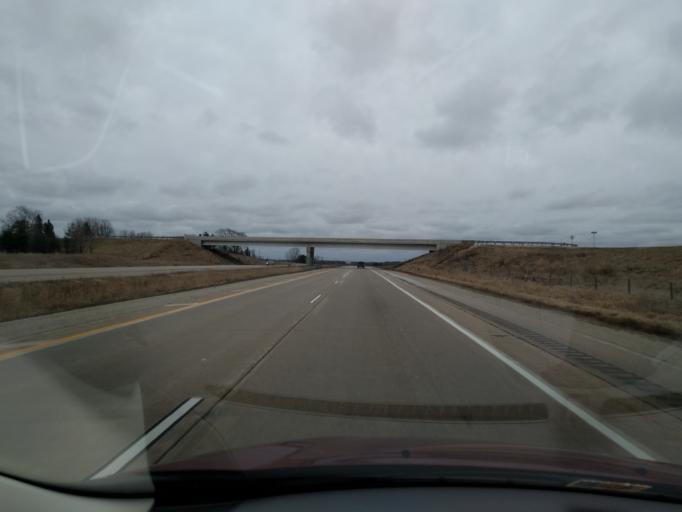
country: US
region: Wisconsin
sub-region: Winnebago County
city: Winneconne
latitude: 44.1850
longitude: -88.6676
